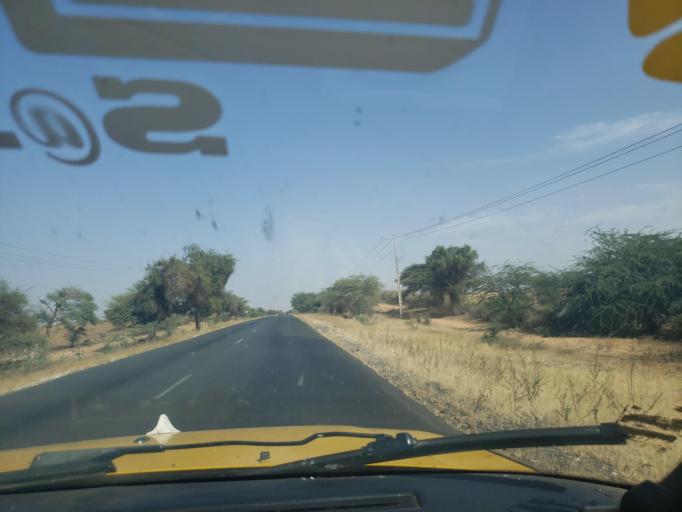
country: SN
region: Saint-Louis
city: Saint-Louis
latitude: 15.9282
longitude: -16.3566
